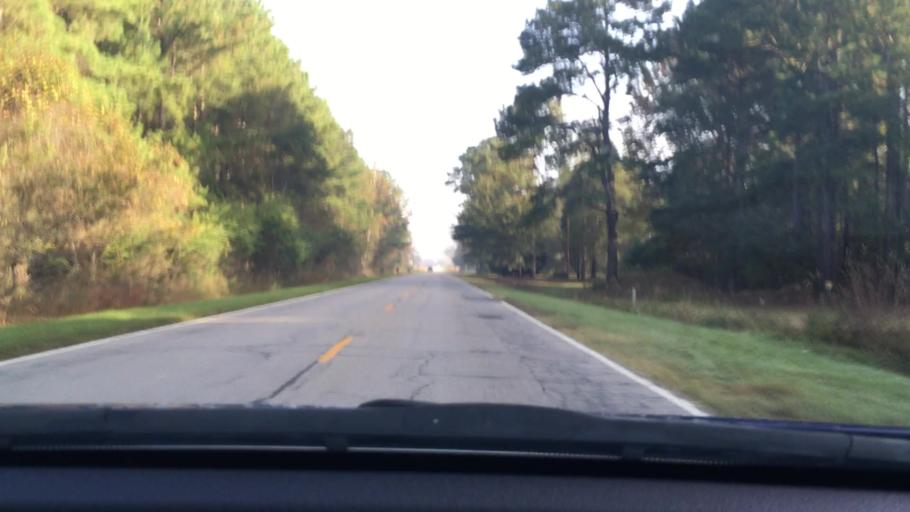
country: US
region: South Carolina
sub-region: Sumter County
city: East Sumter
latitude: 33.9758
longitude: -80.2990
